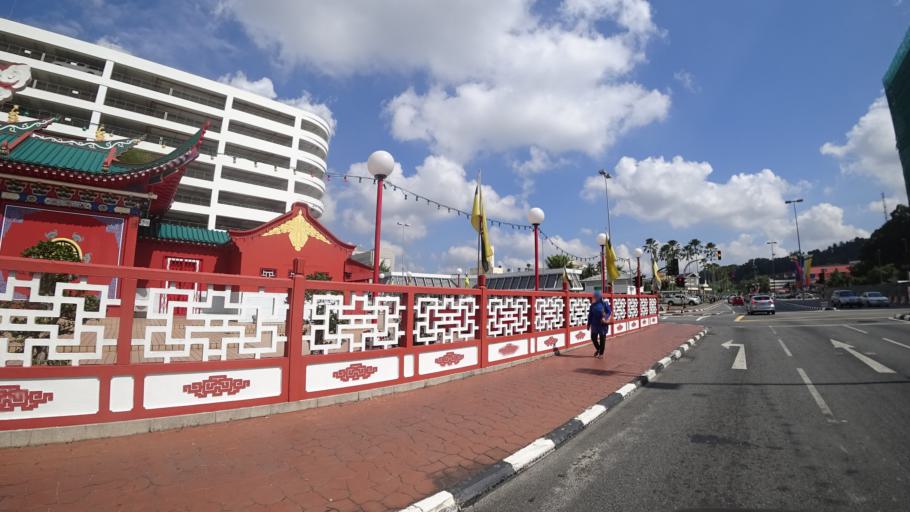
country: BN
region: Brunei and Muara
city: Bandar Seri Begawan
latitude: 4.8901
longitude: 114.9440
